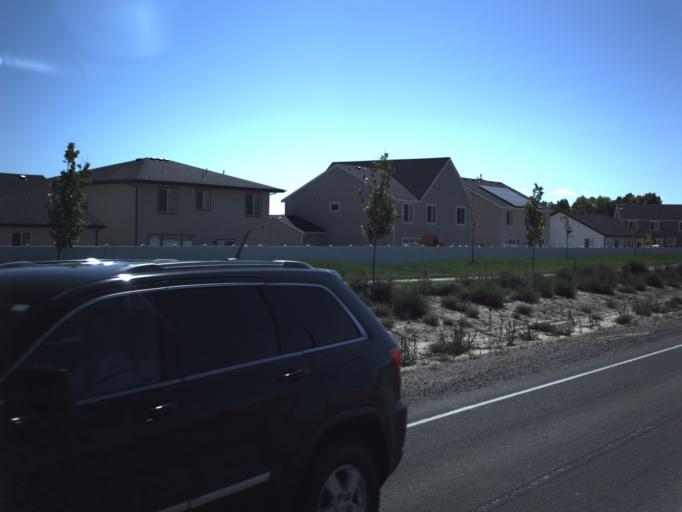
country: US
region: Utah
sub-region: Utah County
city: Saratoga Springs
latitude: 40.3495
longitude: -111.9164
